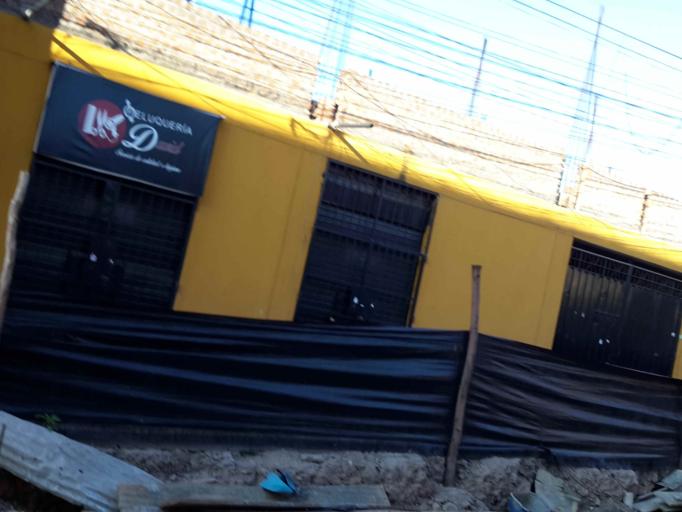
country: PE
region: Ayacucho
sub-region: Provincia de Huamanga
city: Ayacucho
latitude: -13.1544
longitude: -74.2267
